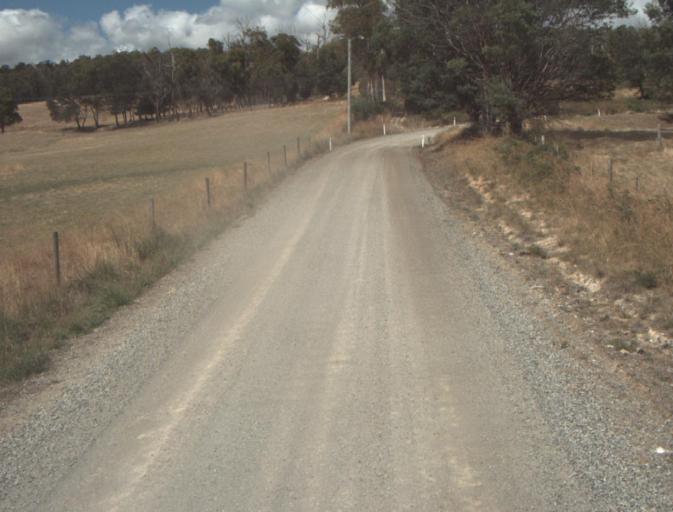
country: AU
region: Tasmania
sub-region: Launceston
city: Mayfield
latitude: -41.2196
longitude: 147.1584
